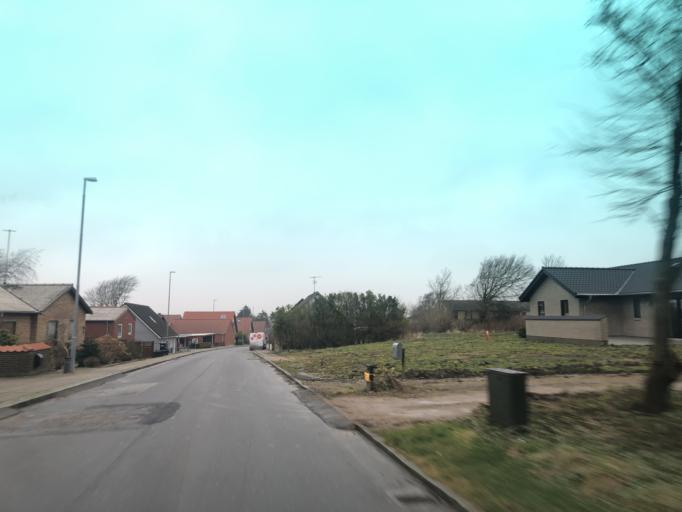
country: DK
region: North Denmark
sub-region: Thisted Kommune
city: Hurup
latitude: 56.7461
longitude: 8.4193
